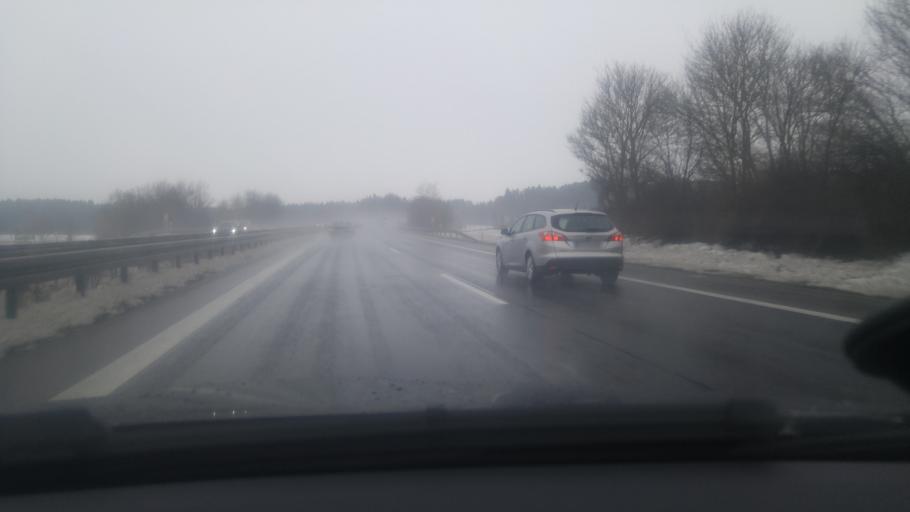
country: DE
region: Baden-Wuerttemberg
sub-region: Freiburg Region
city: Dietingen
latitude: 48.2298
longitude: 8.6503
